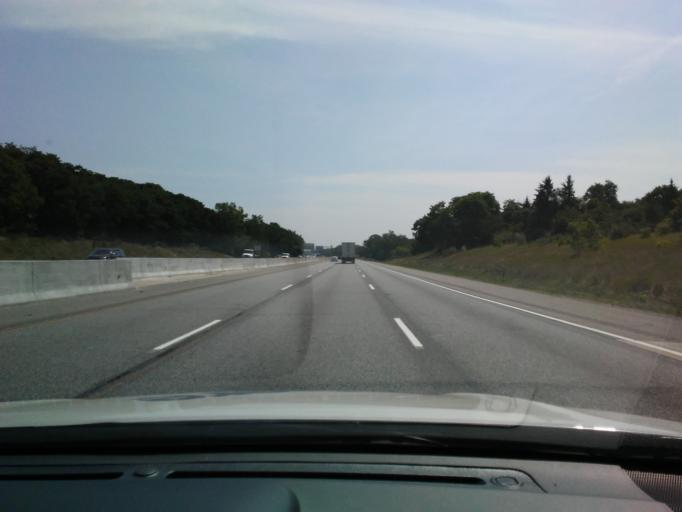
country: US
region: Michigan
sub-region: Livingston County
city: Brighton
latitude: 42.5221
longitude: -83.7401
